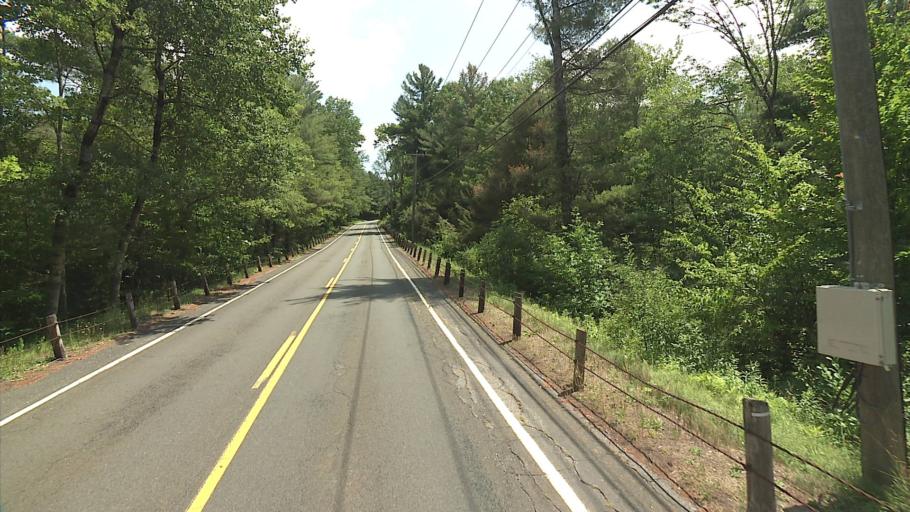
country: US
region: Connecticut
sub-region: Litchfield County
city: Winsted
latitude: 41.9847
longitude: -73.1154
